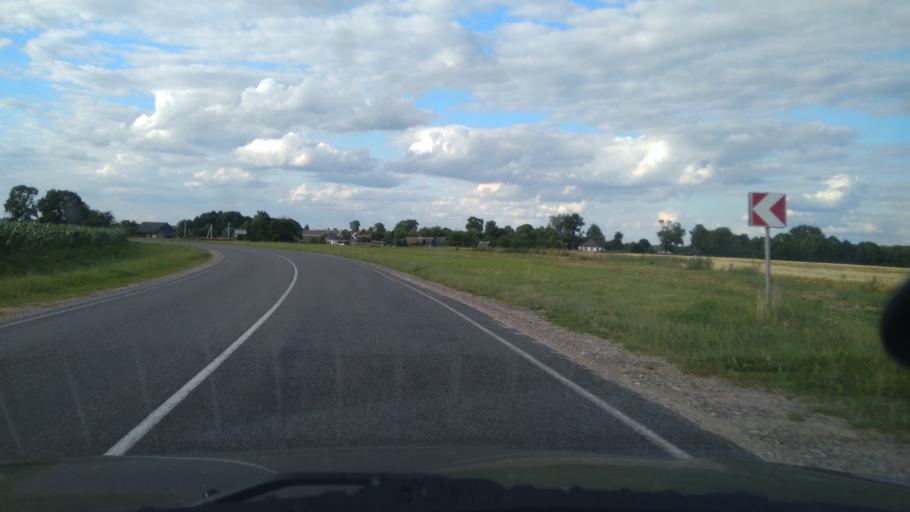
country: BY
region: Grodnenskaya
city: Masty
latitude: 53.3099
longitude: 24.6960
